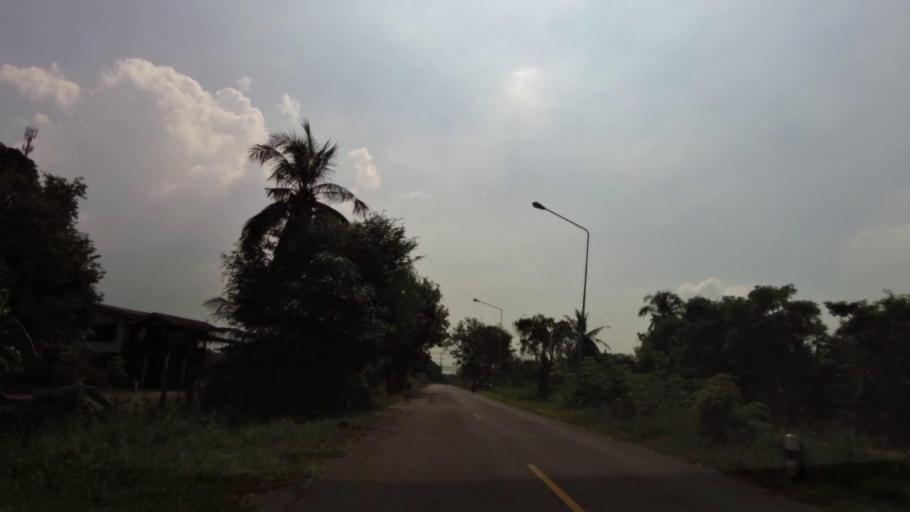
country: TH
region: Ang Thong
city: Ang Thong
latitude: 14.6046
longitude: 100.3963
